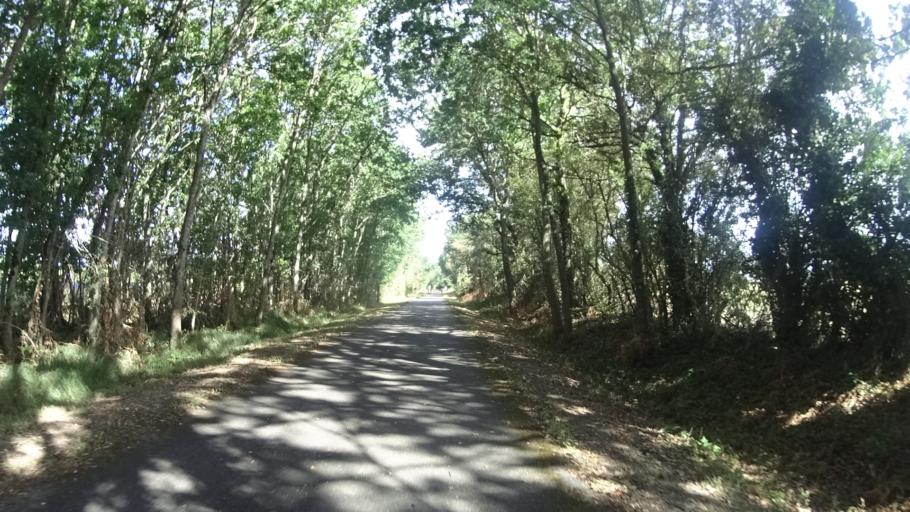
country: FR
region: Bourgogne
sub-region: Departement de Saone-et-Loire
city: Bourbon-Lancy
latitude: 46.6153
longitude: 3.7419
